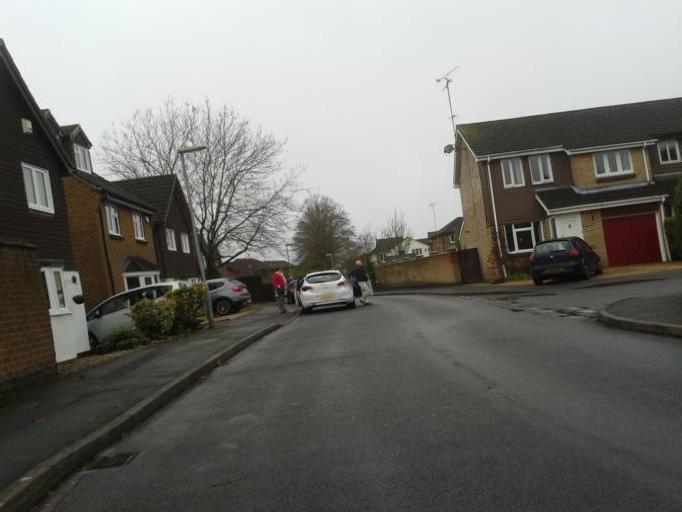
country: GB
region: England
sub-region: Hampshire
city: Farnborough
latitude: 51.2909
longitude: -0.7910
